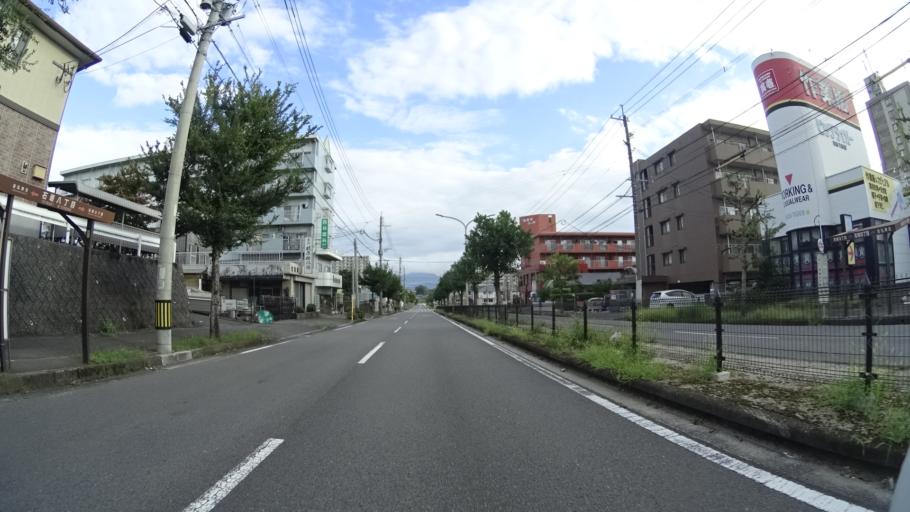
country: JP
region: Oita
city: Beppu
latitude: 33.3013
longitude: 131.4950
